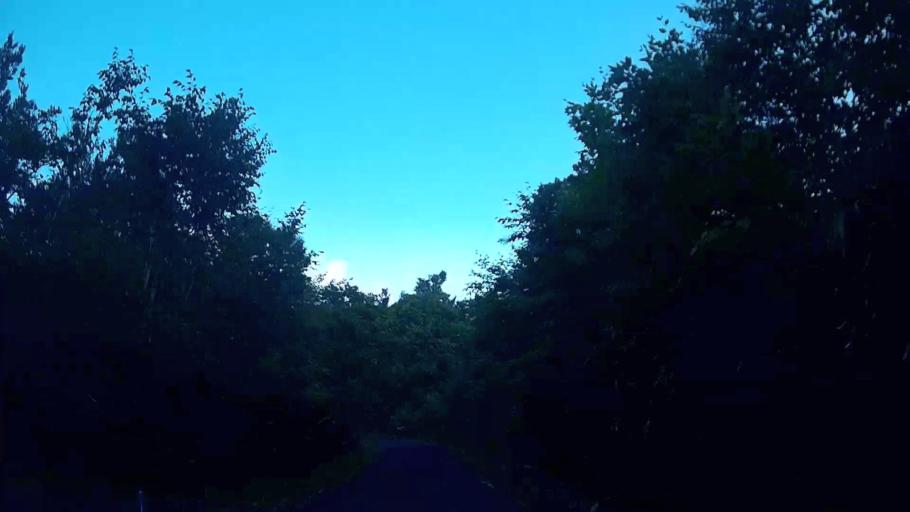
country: JP
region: Hokkaido
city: Iwanai
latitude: 42.6004
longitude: 139.9902
